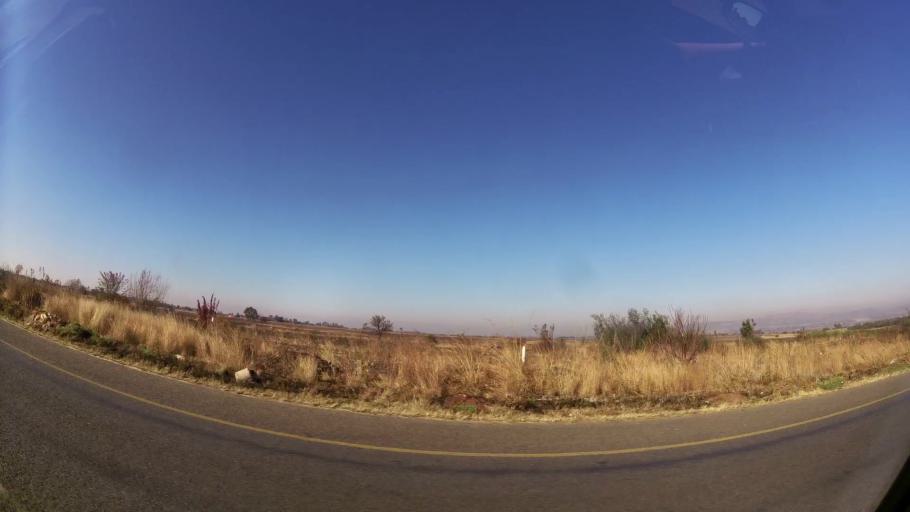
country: ZA
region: Gauteng
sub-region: City of Johannesburg Metropolitan Municipality
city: Johannesburg
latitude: -26.3129
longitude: 28.0762
